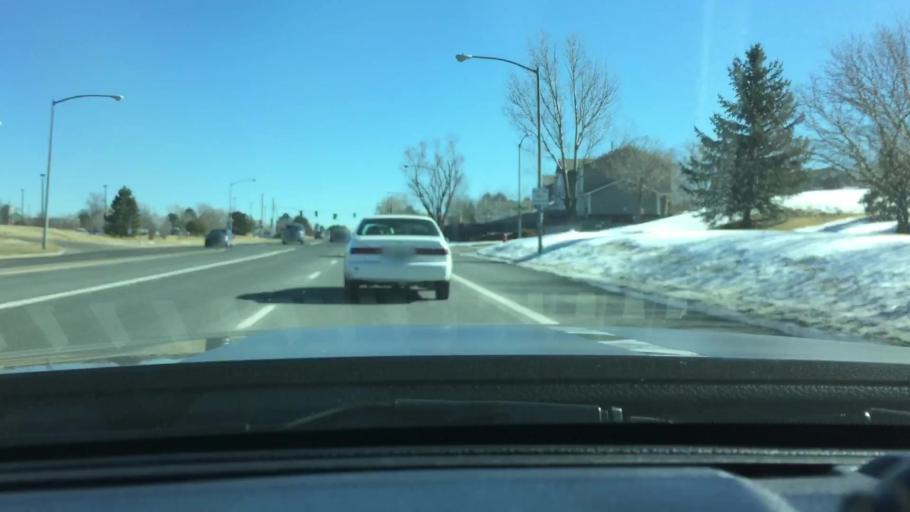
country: US
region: Colorado
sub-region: Broomfield County
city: Broomfield
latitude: 39.8998
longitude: -105.0430
